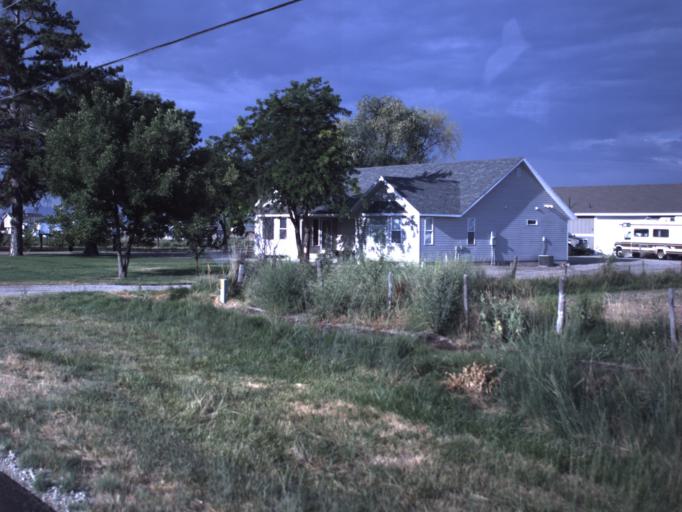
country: US
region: Utah
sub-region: Weber County
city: West Haven
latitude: 41.2256
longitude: -112.0929
